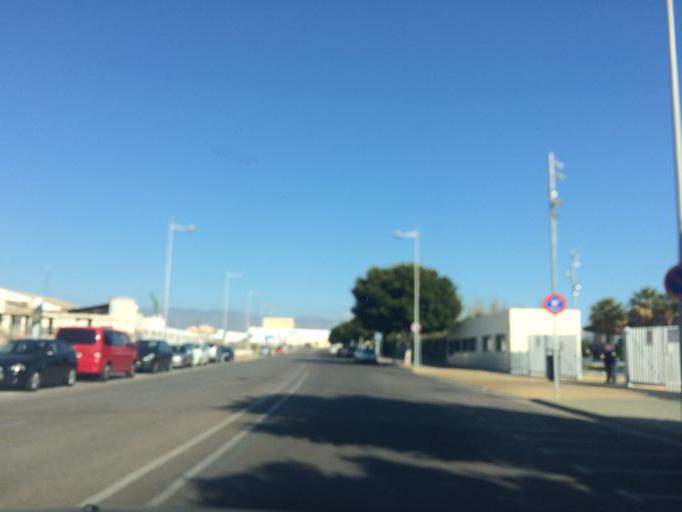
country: ES
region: Andalusia
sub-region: Provincia de Almeria
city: Almeria
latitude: 36.8401
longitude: -2.4377
